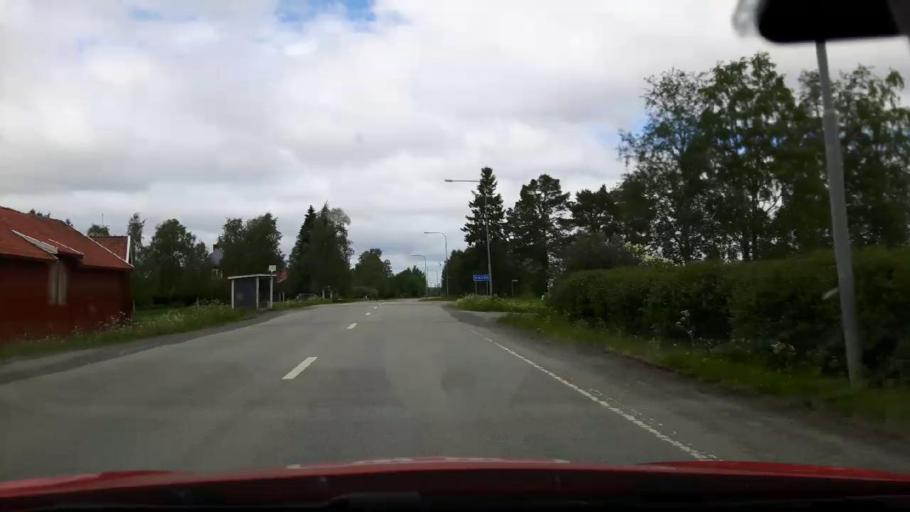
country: SE
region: Jaemtland
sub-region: Krokoms Kommun
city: Krokom
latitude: 63.3111
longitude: 14.4598
